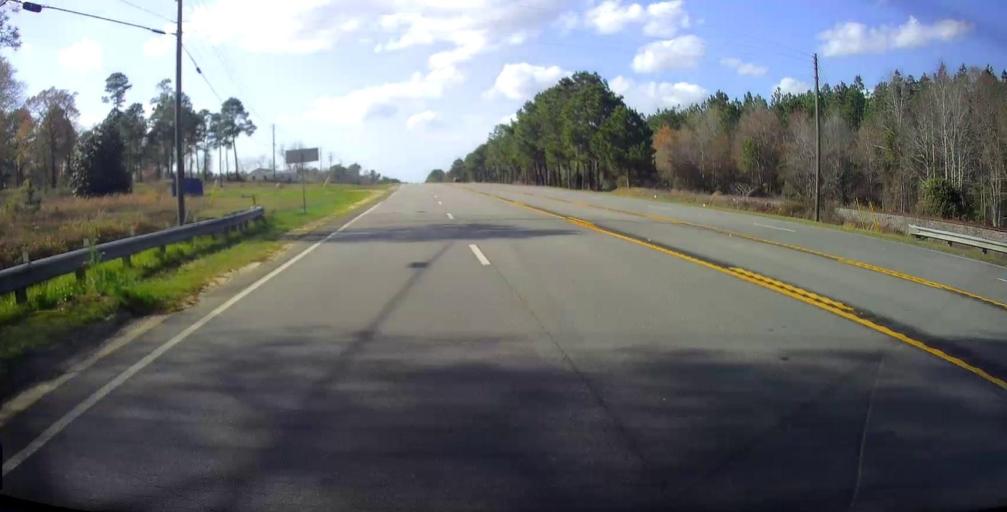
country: US
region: Georgia
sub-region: Telfair County
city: Helena
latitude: 32.0805
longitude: -82.9237
